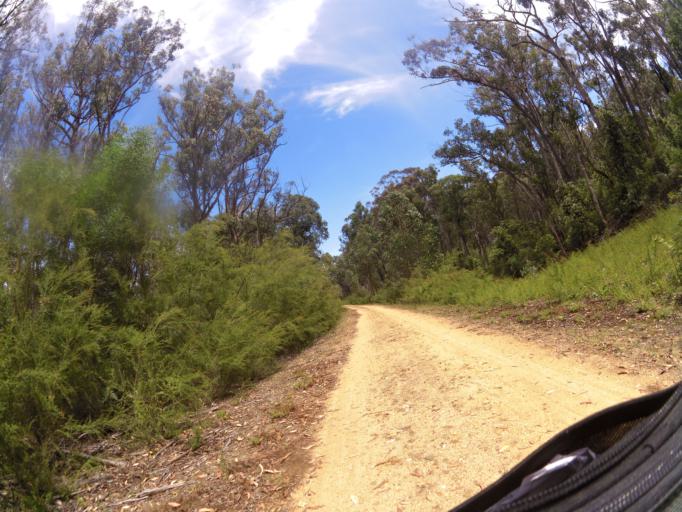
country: AU
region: Victoria
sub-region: East Gippsland
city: Lakes Entrance
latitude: -37.7442
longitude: 147.9993
